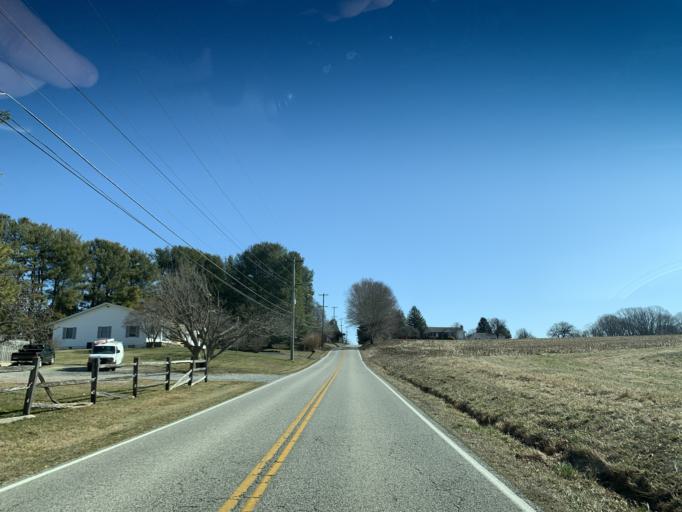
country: US
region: Maryland
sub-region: Cecil County
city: Rising Sun
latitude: 39.6357
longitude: -76.1066
